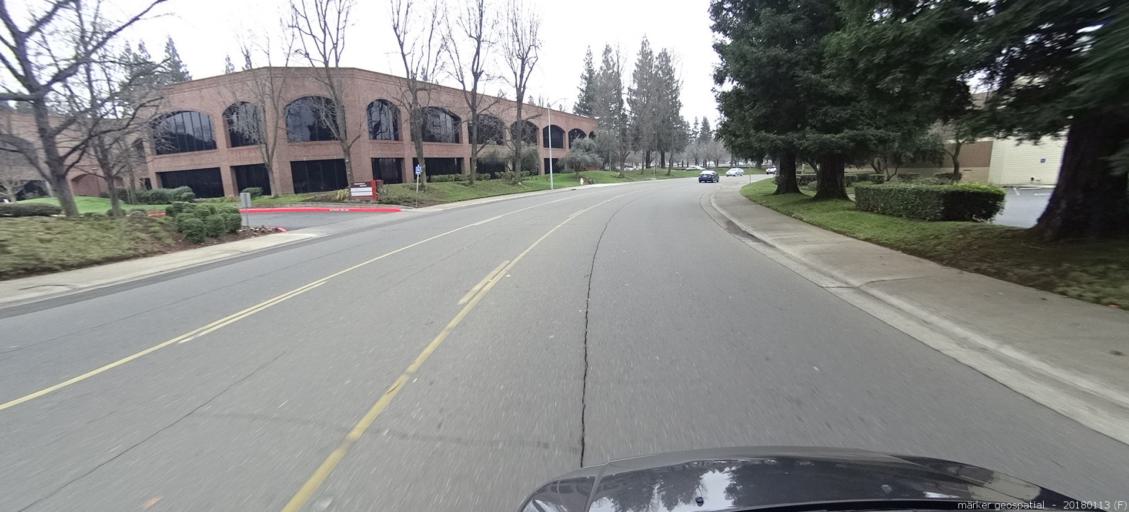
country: US
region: California
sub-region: Sacramento County
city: Rancho Cordova
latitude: 38.5975
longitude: -121.2808
